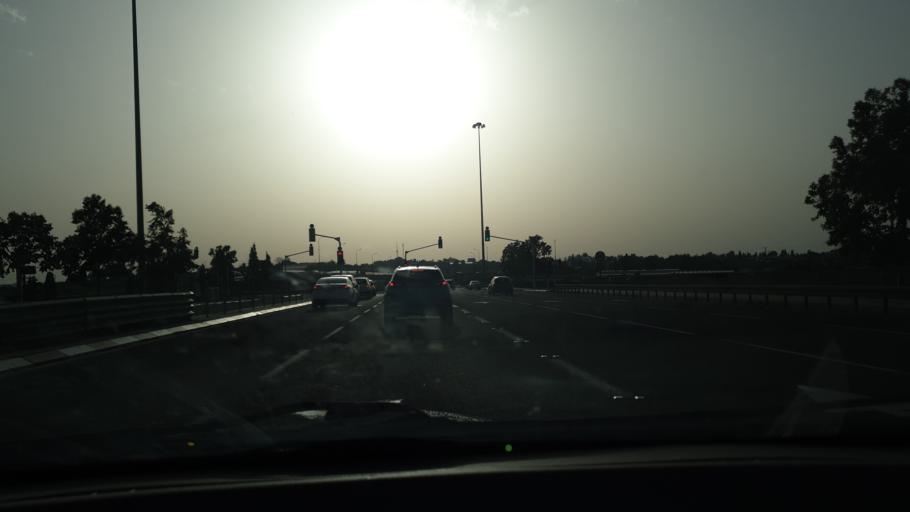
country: IL
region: Central District
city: Even Yehuda
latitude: 32.2552
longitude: 34.8898
